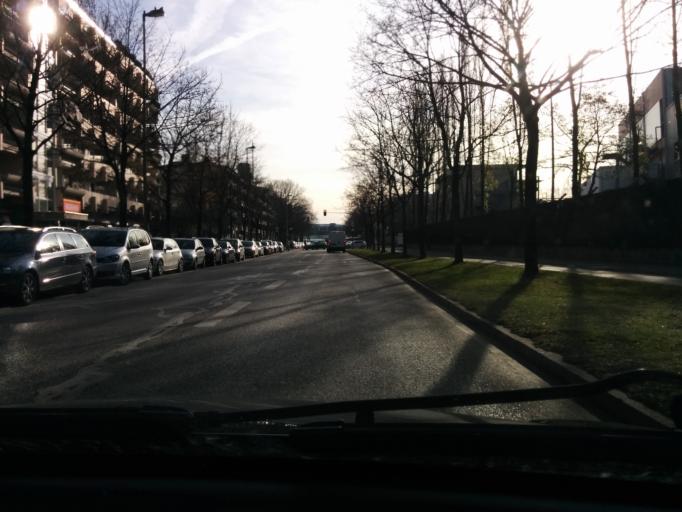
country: DE
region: Bavaria
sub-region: Upper Bavaria
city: Munich
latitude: 48.1785
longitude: 11.5643
